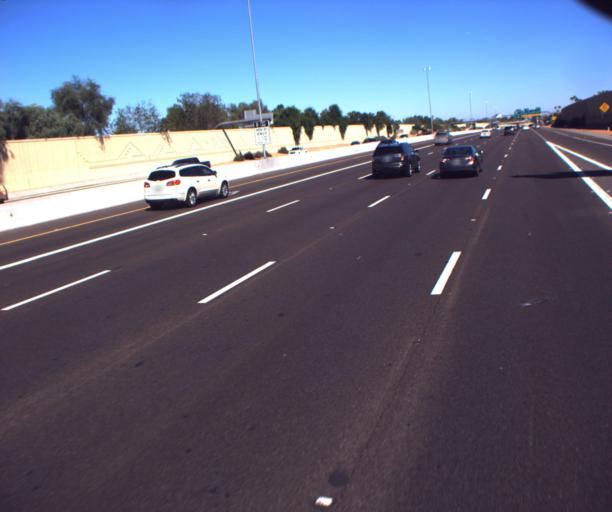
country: US
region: Arizona
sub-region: Maricopa County
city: San Carlos
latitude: 33.3685
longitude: -111.8935
